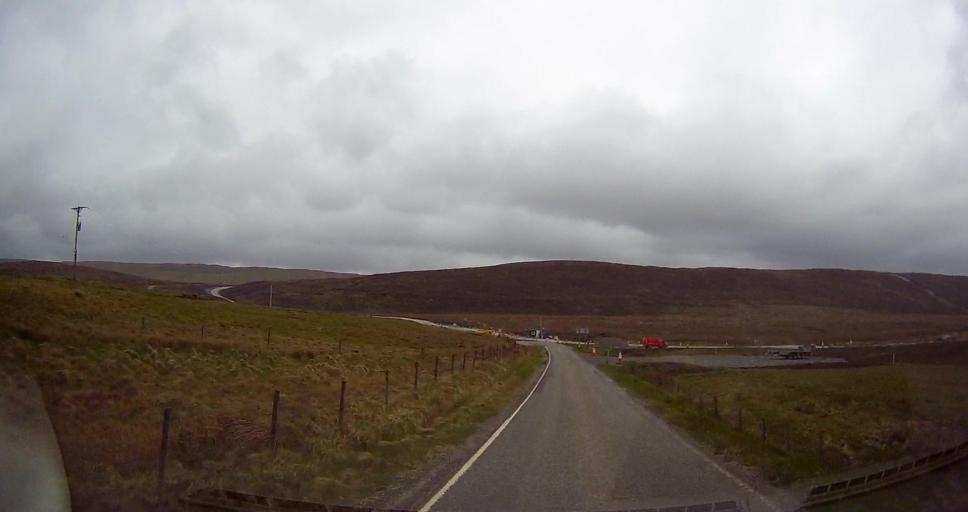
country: GB
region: Scotland
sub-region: Shetland Islands
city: Lerwick
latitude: 60.2791
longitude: -1.2457
